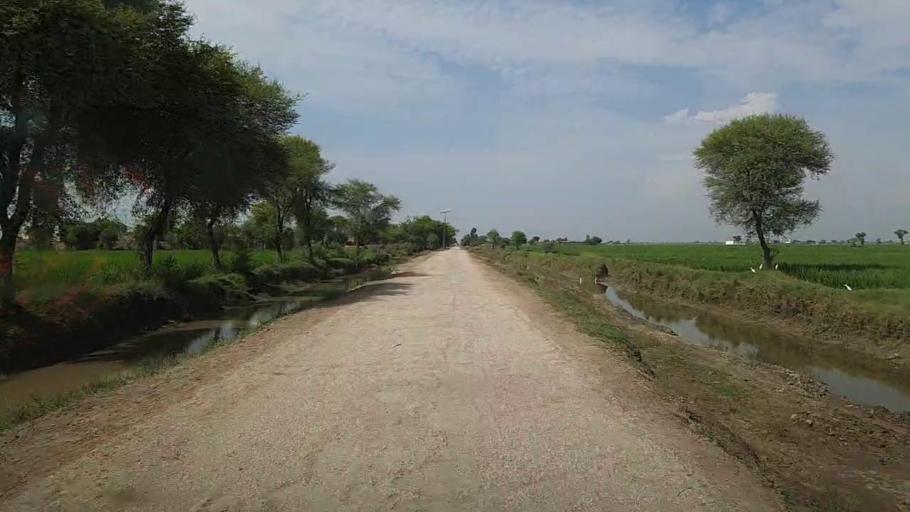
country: PK
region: Sindh
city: Thul
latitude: 28.2491
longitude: 68.8085
